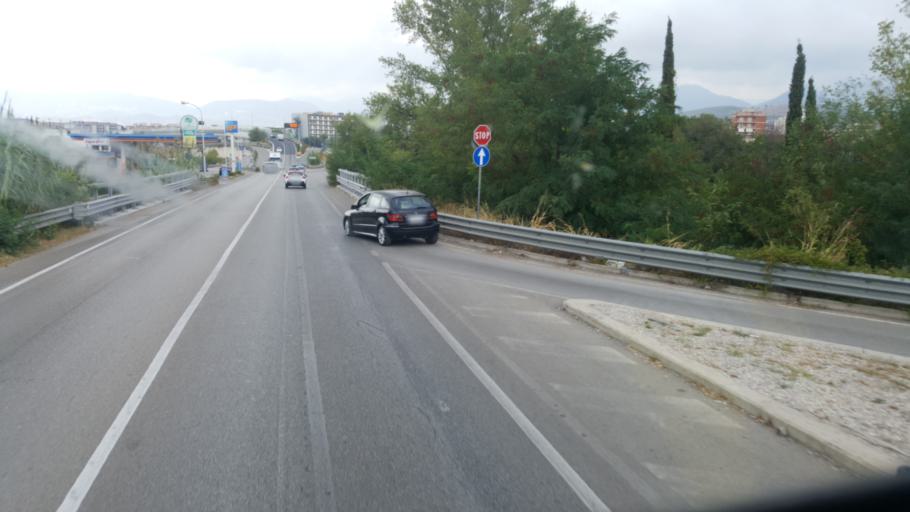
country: IT
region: Campania
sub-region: Provincia di Salerno
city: Battipaglia
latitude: 40.6096
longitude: 14.9729
